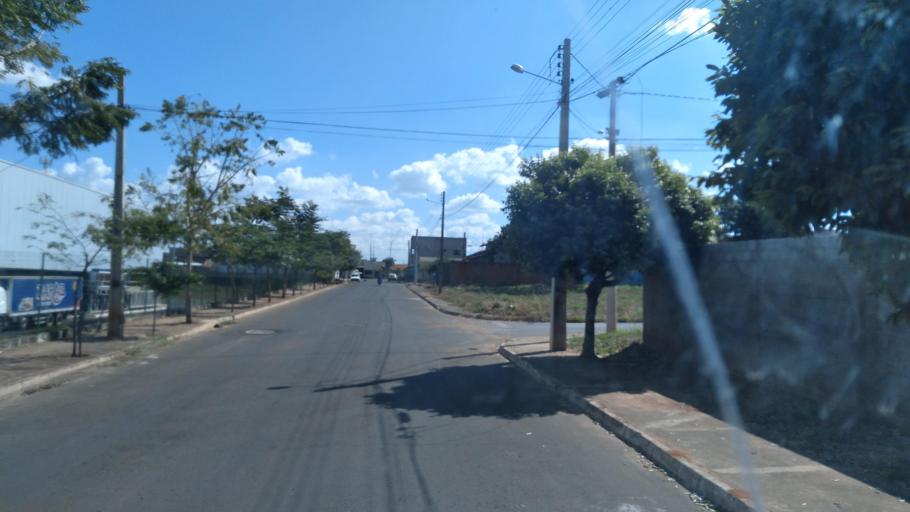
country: BR
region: Goias
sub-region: Mineiros
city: Mineiros
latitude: -17.5490
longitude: -52.5433
